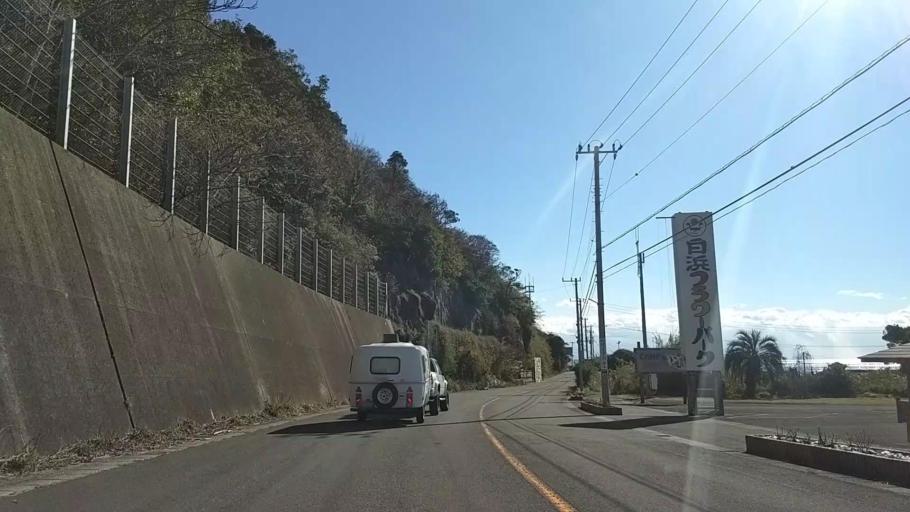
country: JP
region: Chiba
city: Tateyama
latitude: 34.9108
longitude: 139.8293
